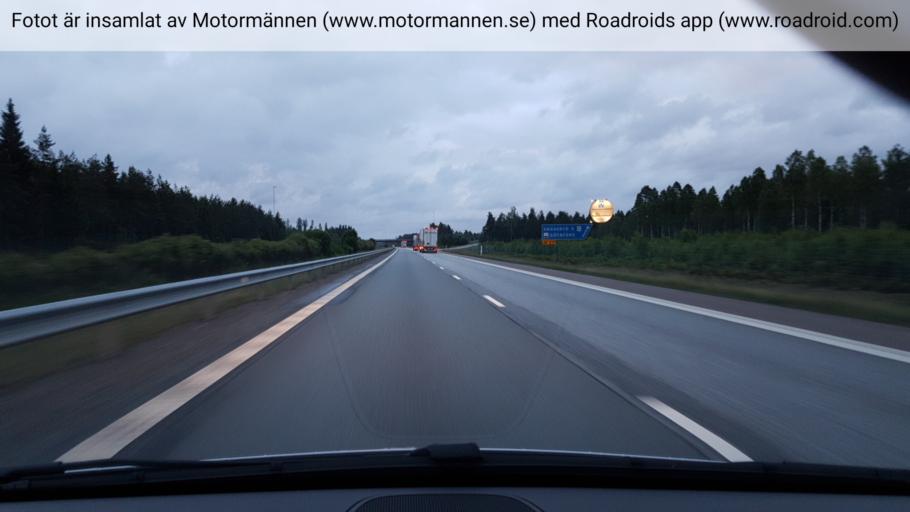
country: SE
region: Joenkoeping
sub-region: Vaggeryds Kommun
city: Vaggeryd
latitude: 57.4875
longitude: 14.1041
